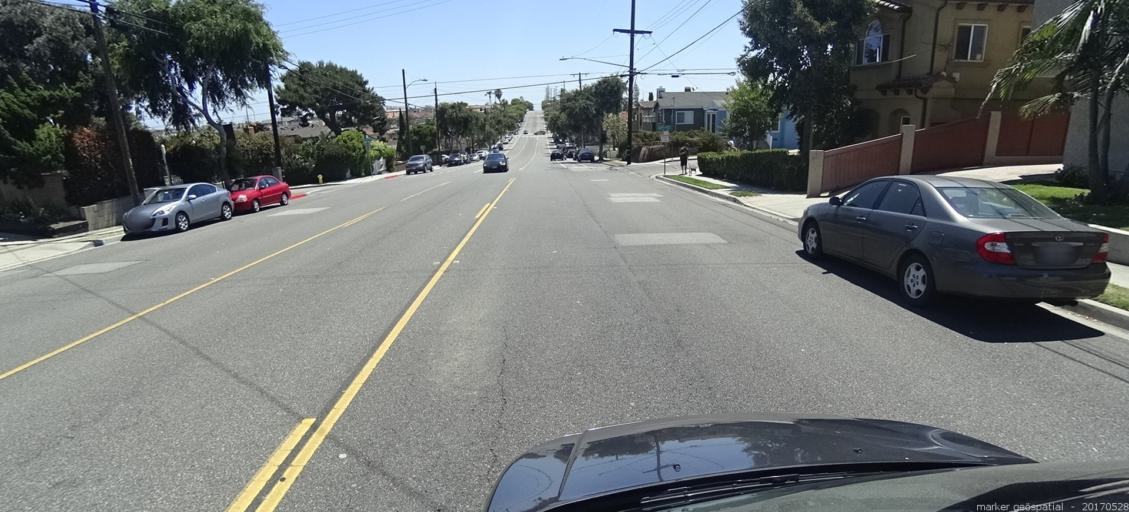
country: US
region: California
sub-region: Los Angeles County
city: Hermosa Beach
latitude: 33.8690
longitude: -118.3816
